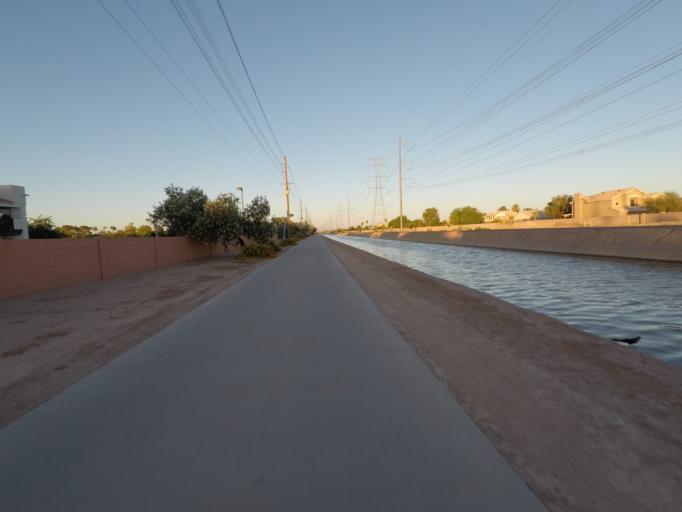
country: US
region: Arizona
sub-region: Maricopa County
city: Guadalupe
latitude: 33.3567
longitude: -111.9100
